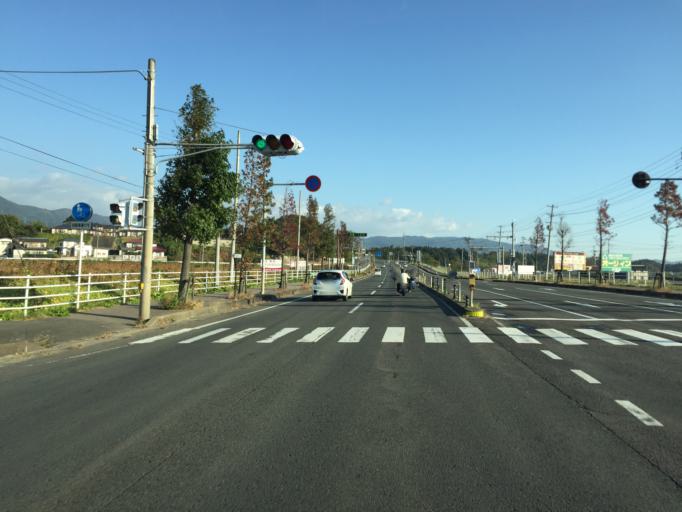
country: JP
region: Fukushima
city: Hobaramachi
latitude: 37.8369
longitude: 140.5198
